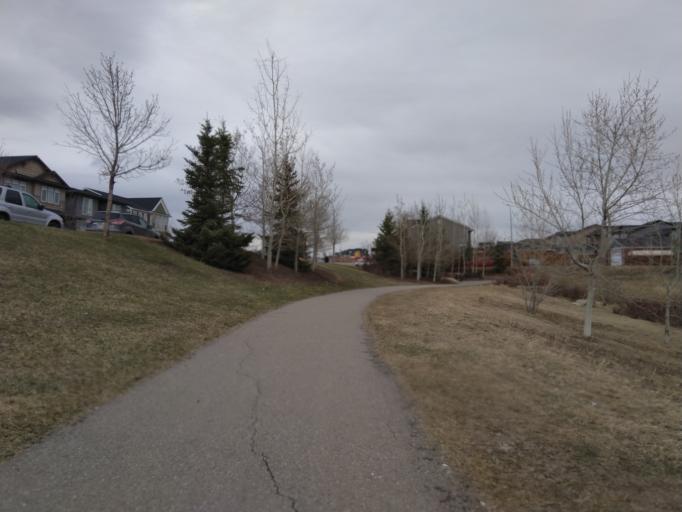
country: CA
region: Alberta
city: Calgary
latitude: 51.1745
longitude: -114.1037
